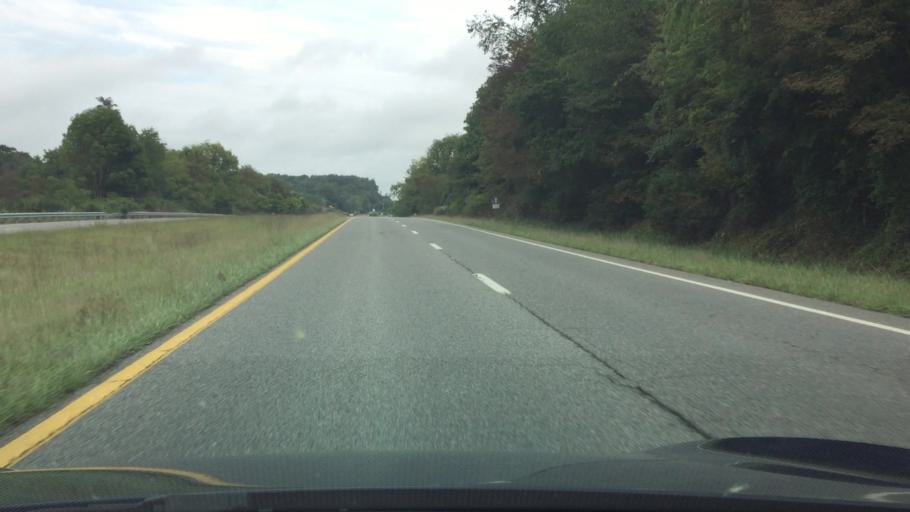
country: US
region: Virginia
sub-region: City of Radford
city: Radford
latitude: 37.1153
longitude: -80.5280
